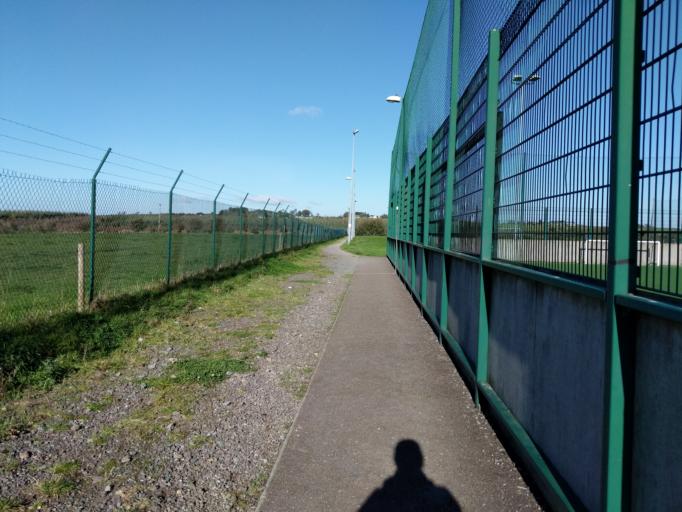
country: IE
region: Munster
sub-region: County Cork
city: Blarney
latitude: 51.9821
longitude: -8.5344
